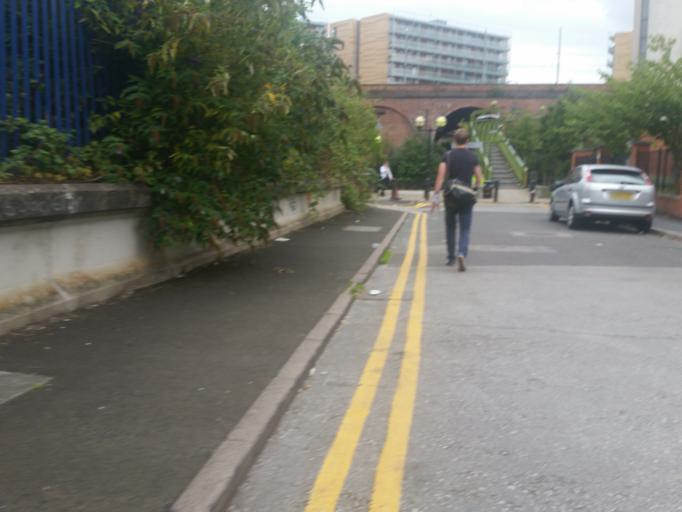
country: GB
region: England
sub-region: Manchester
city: Hulme
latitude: 53.4732
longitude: -2.2663
